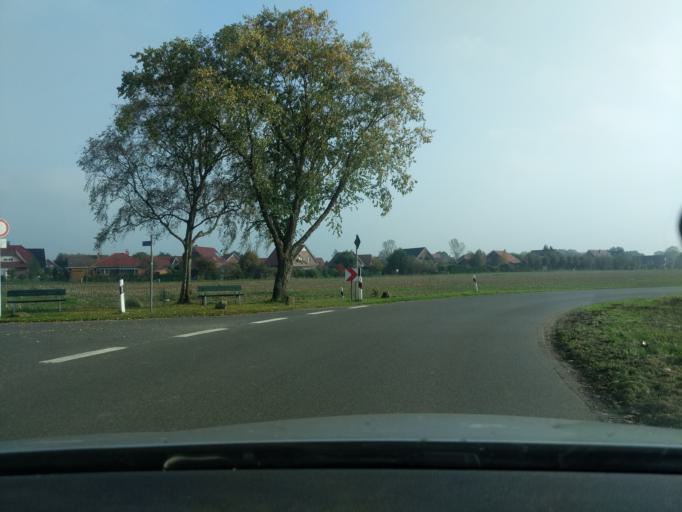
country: DE
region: Lower Saxony
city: Wanna
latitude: 53.7420
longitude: 8.7862
